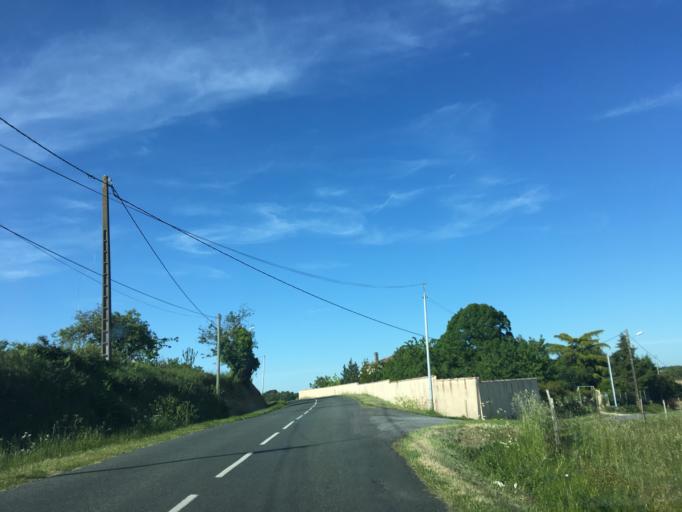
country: FR
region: Poitou-Charentes
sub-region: Departement de la Charente-Maritime
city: Mirambeau
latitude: 45.3465
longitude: -0.5862
